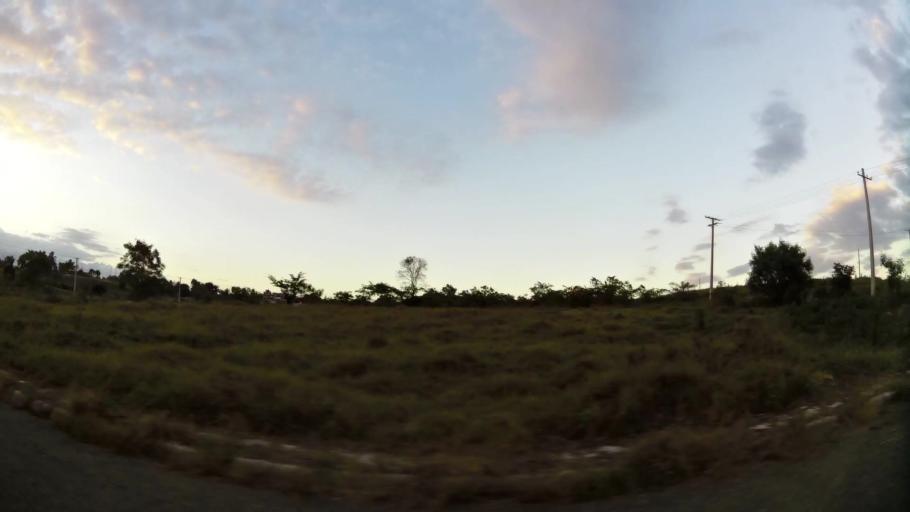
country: DO
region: Nacional
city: La Agustina
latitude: 18.5663
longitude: -69.9361
